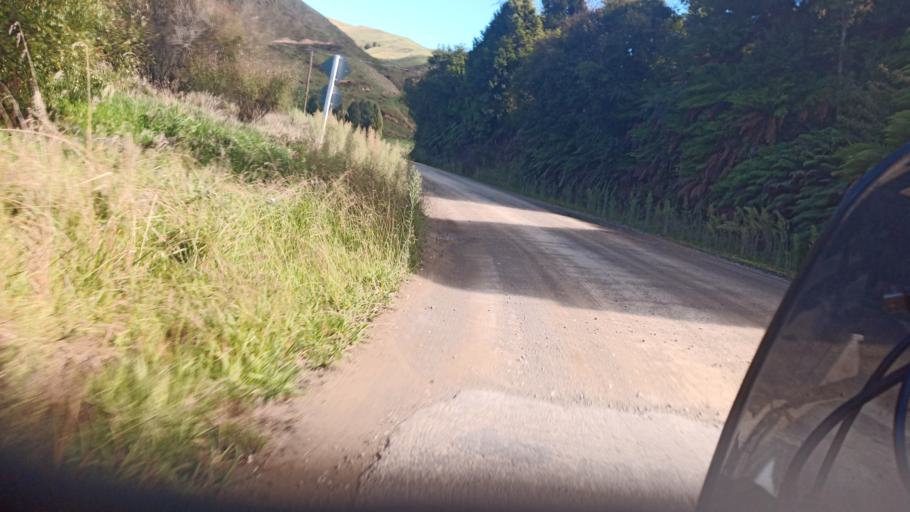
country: NZ
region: Bay of Plenty
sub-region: Opotiki District
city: Opotiki
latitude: -38.2971
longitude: 177.5542
